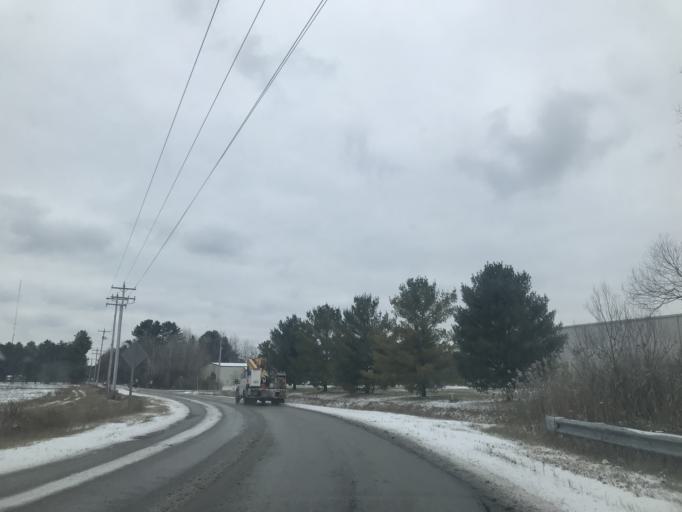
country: US
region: Wisconsin
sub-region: Marinette County
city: Marinette
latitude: 45.0716
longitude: -87.6595
